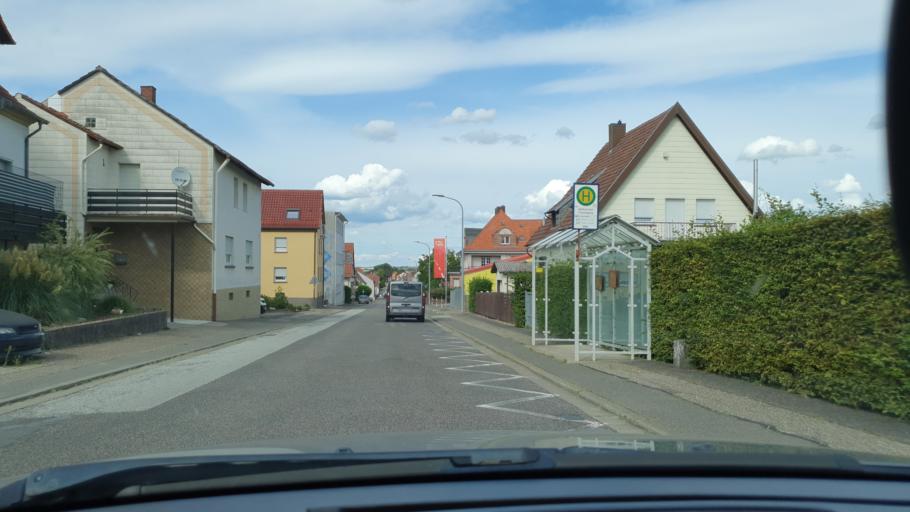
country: DE
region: Rheinland-Pfalz
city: Hohfroschen
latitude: 49.2443
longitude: 7.5614
